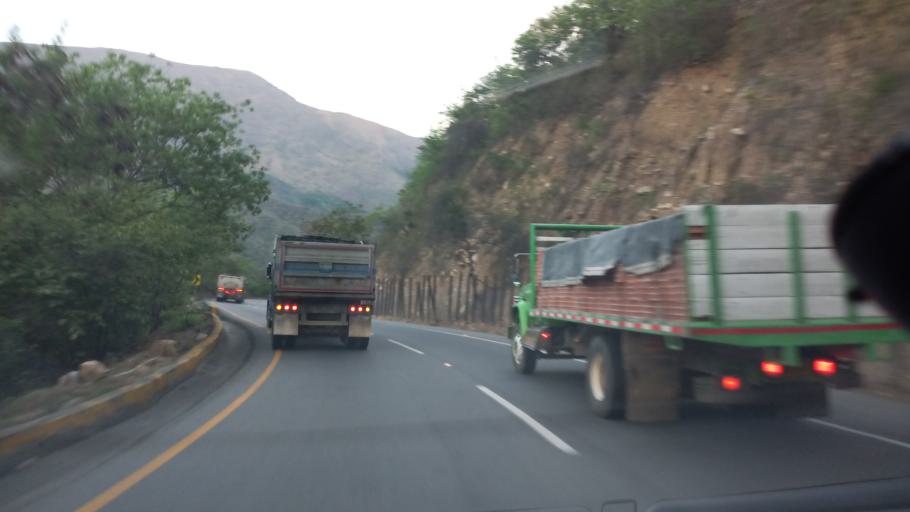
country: CO
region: Cundinamarca
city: Pandi
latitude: 4.2561
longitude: -74.5325
